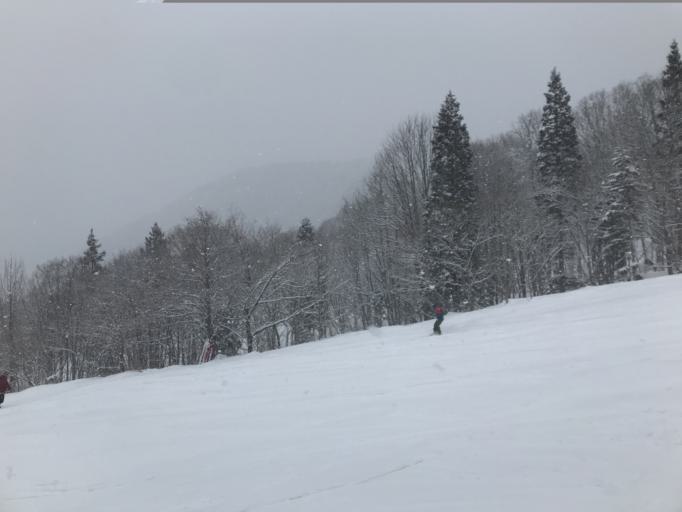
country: JP
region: Nagano
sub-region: Kitaazumi Gun
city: Hakuba
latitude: 36.7542
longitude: 137.8476
